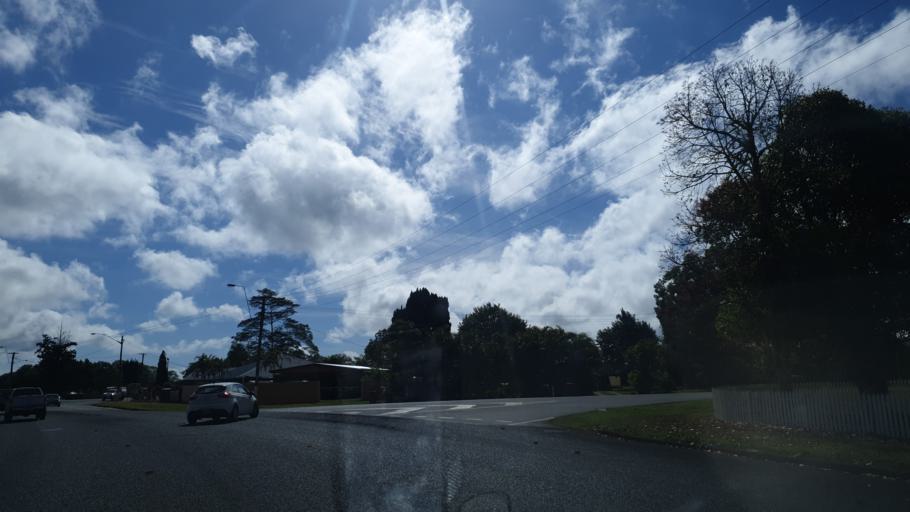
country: AU
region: Queensland
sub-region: Tablelands
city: Atherton
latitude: -17.3519
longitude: 145.5909
